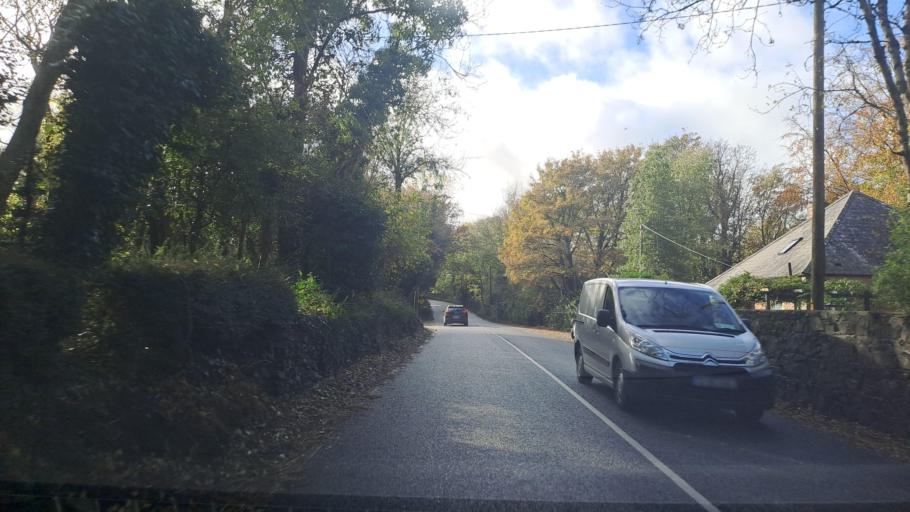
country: IE
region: Ulster
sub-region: County Monaghan
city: Monaghan
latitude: 54.2185
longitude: -6.9822
